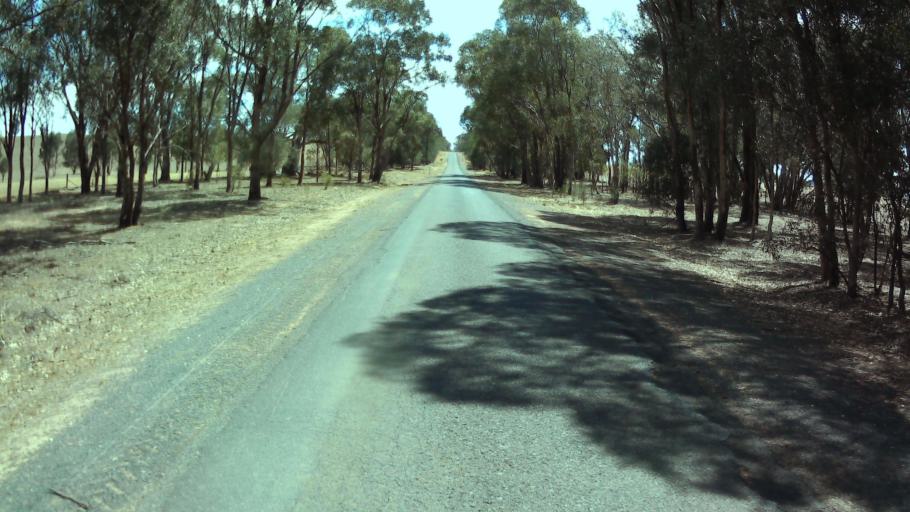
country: AU
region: New South Wales
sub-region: Weddin
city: Grenfell
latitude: -33.7636
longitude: 148.2046
